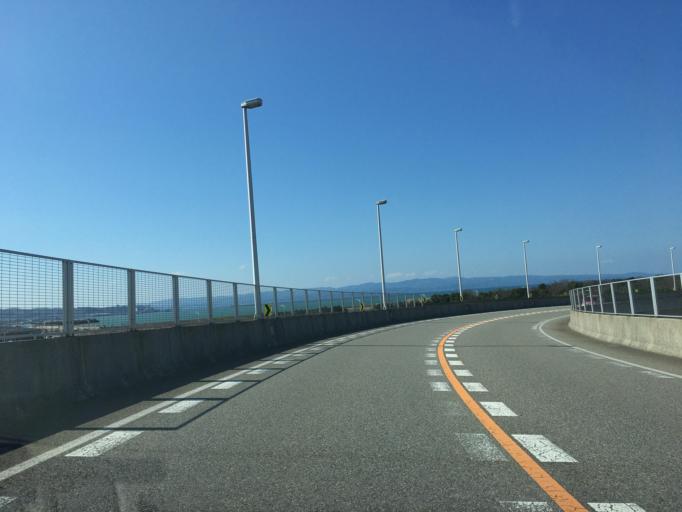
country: JP
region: Toyama
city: Nishishinminato
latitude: 36.7801
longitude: 137.1044
